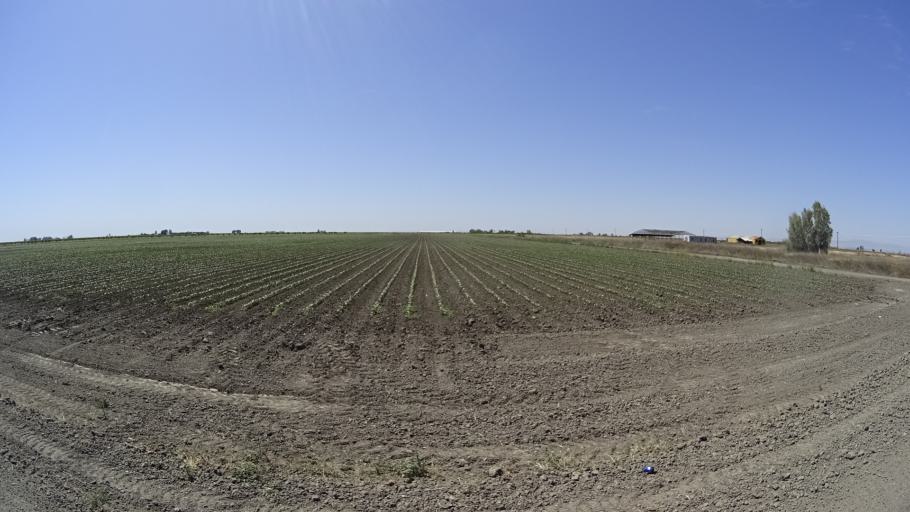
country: US
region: California
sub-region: Kings County
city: Stratford
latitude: 36.1895
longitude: -119.7956
